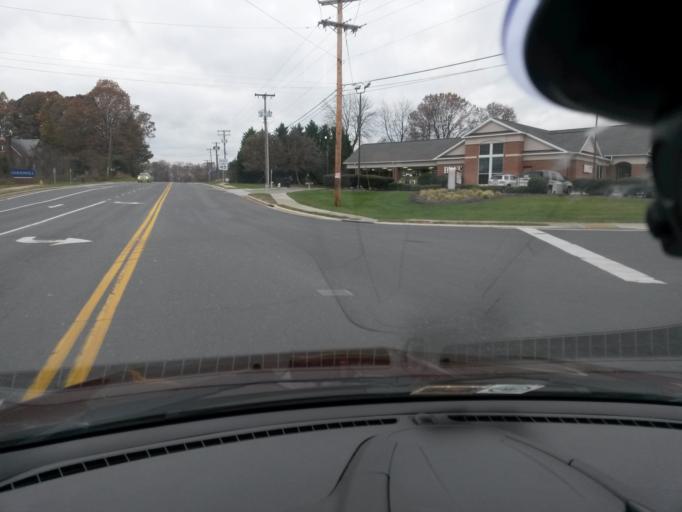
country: US
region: Virginia
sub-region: Amherst County
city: Madison Heights
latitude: 37.4665
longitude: -79.1192
